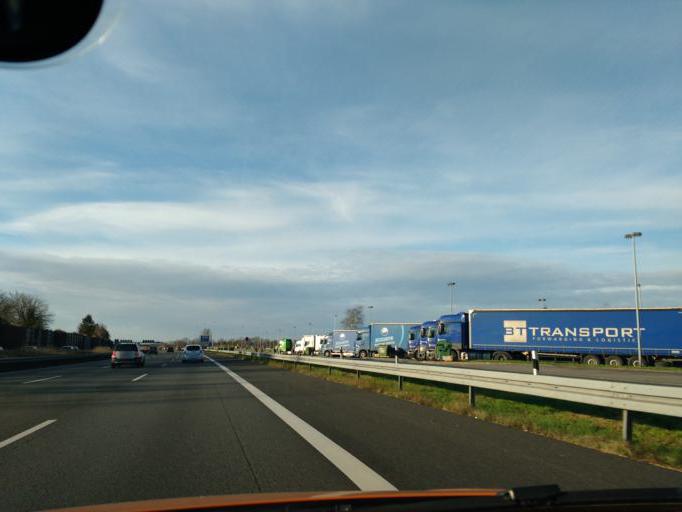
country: DE
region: Lower Saxony
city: Lehrte
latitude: 52.3883
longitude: 9.9952
